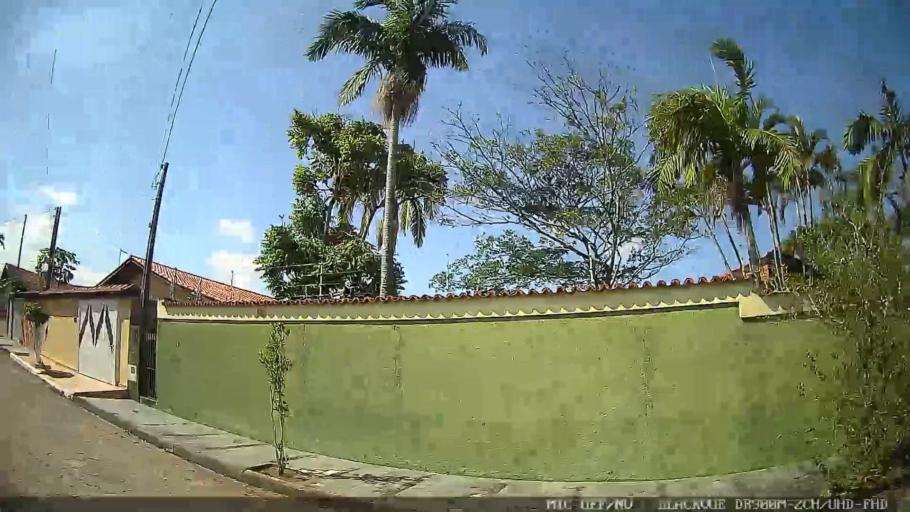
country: BR
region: Sao Paulo
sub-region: Peruibe
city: Peruibe
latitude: -24.3106
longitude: -46.9965
